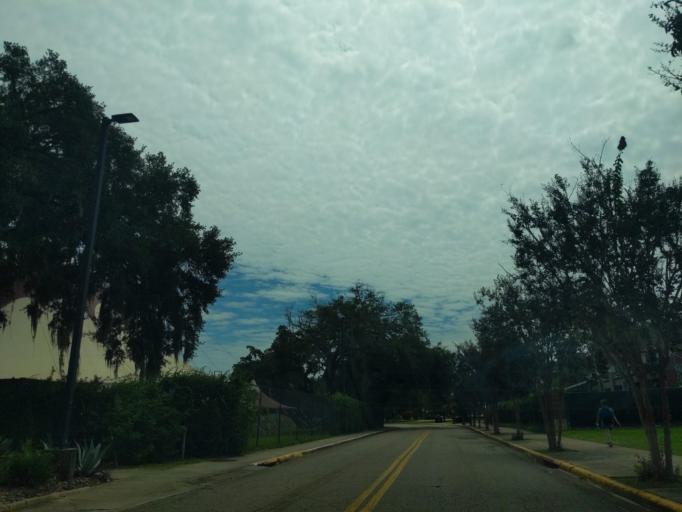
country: US
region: Florida
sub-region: Leon County
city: Tallahassee
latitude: 30.4413
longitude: -84.3030
